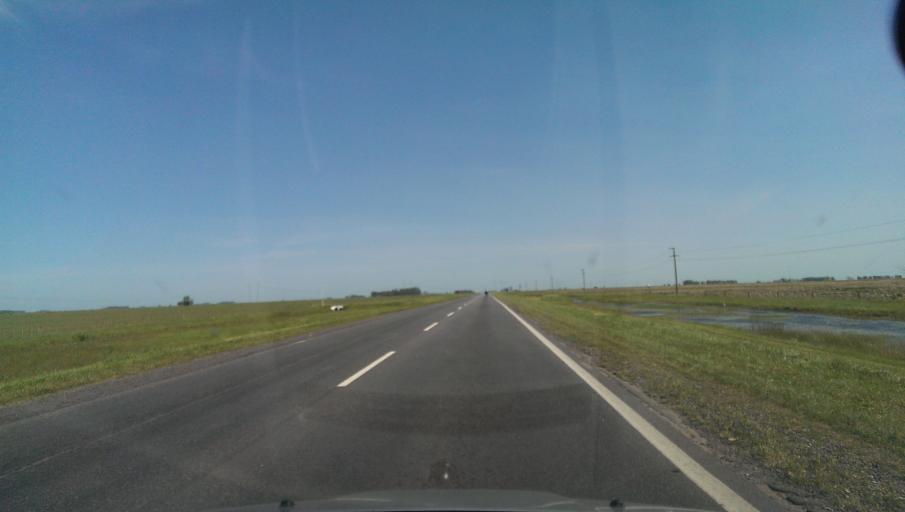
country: AR
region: Buenos Aires
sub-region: Partido de Azul
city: Azul
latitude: -36.5758
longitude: -59.6431
